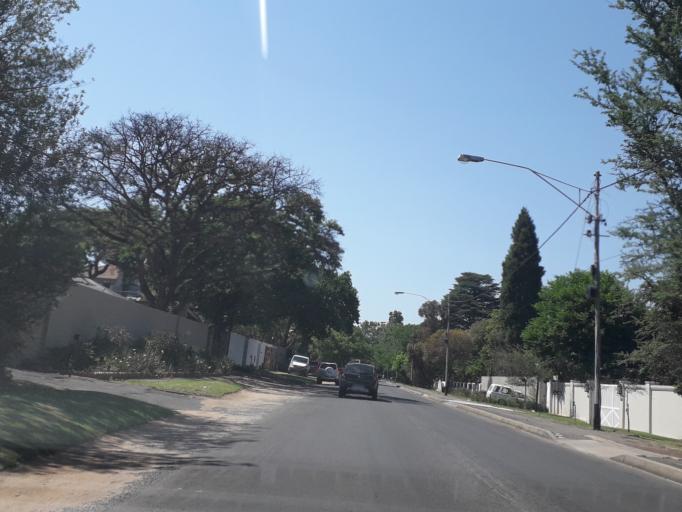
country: ZA
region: Gauteng
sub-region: City of Johannesburg Metropolitan Municipality
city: Johannesburg
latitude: -26.1298
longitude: 28.0240
